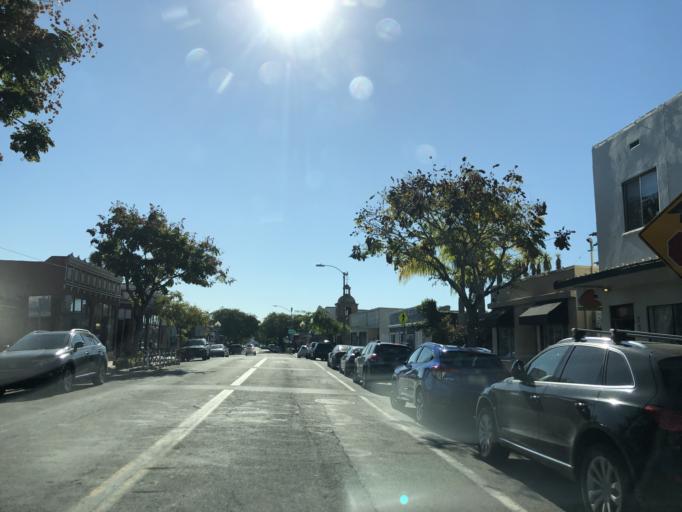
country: US
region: California
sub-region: San Diego County
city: San Diego
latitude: 32.7307
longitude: -117.1296
